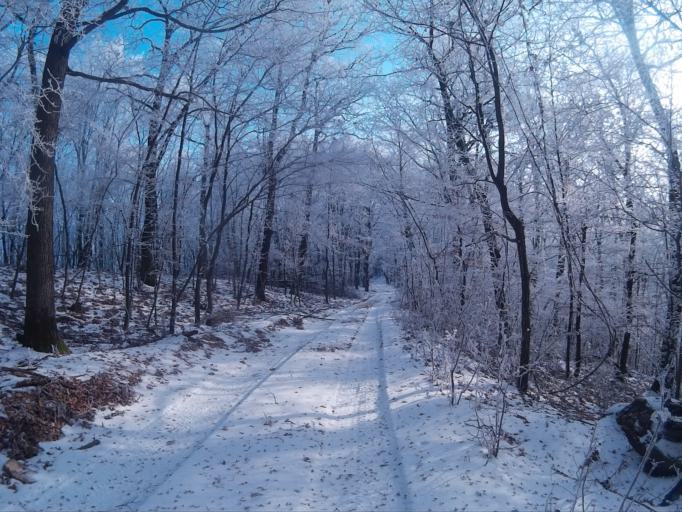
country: HU
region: Borsod-Abauj-Zemplen
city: Szendro
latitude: 48.4924
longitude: 20.7417
